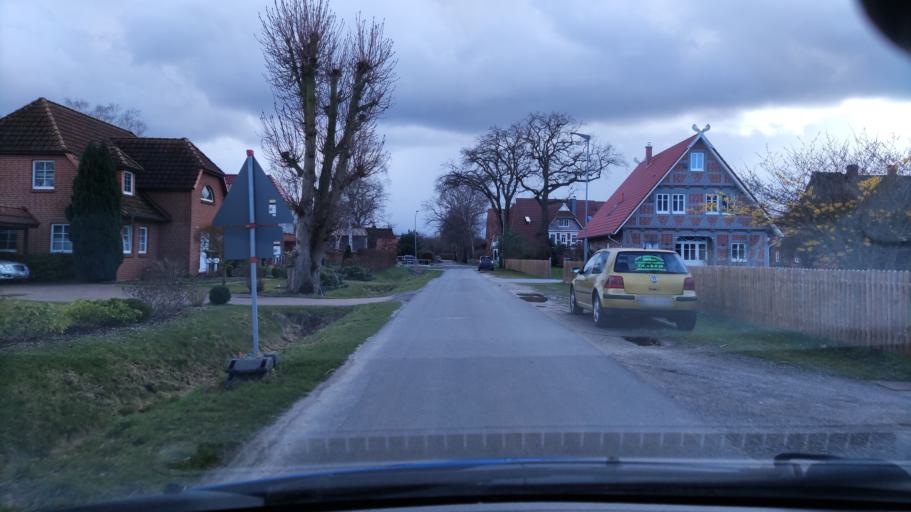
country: DE
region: Lower Saxony
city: Winsen
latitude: 53.3424
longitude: 10.1965
